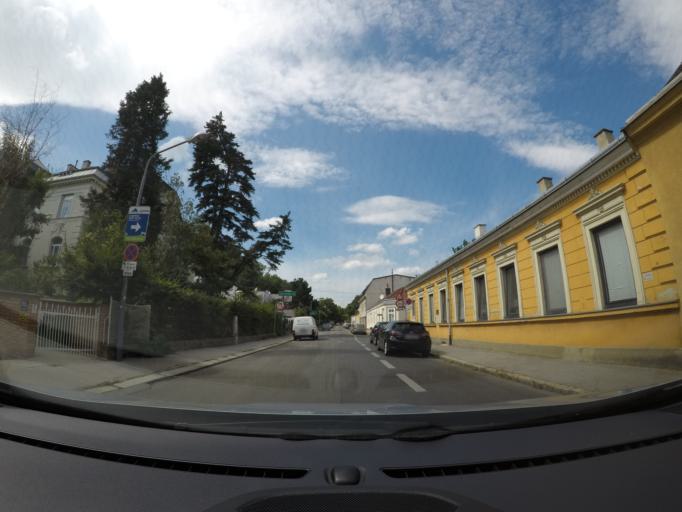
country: AT
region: Lower Austria
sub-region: Politischer Bezirk Wien-Umgebung
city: Purkersdorf
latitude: 48.1985
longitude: 16.2544
